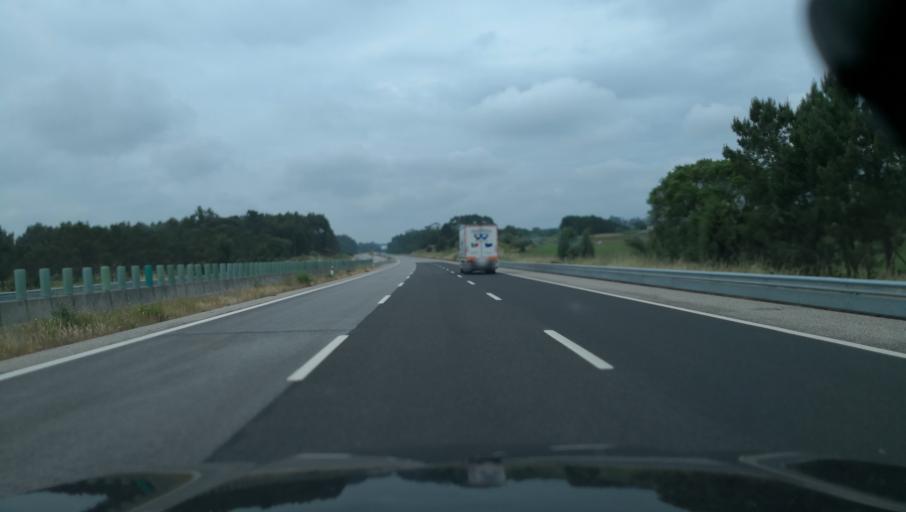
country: PT
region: Coimbra
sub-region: Figueira da Foz
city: Lavos
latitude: 40.0904
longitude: -8.7621
